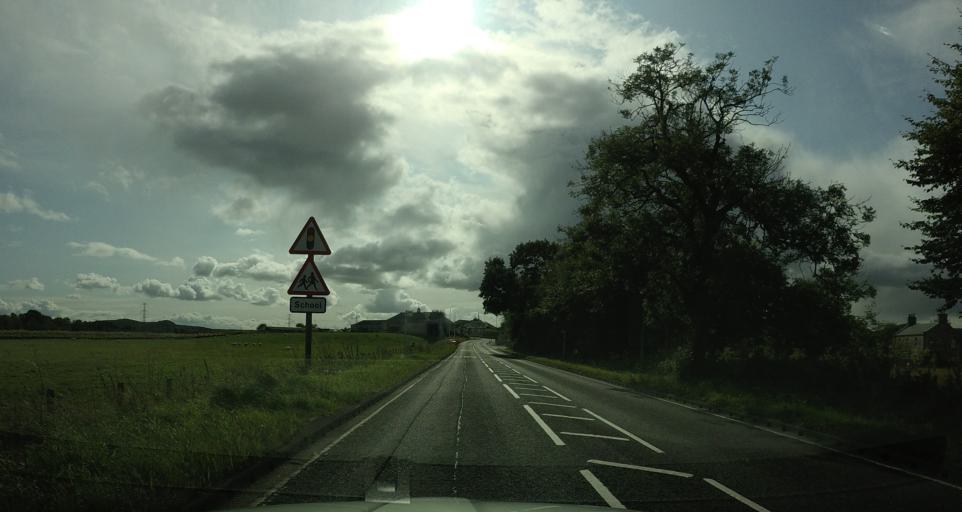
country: GB
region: Scotland
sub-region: Fife
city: Saline
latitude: 56.1857
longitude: -3.5497
